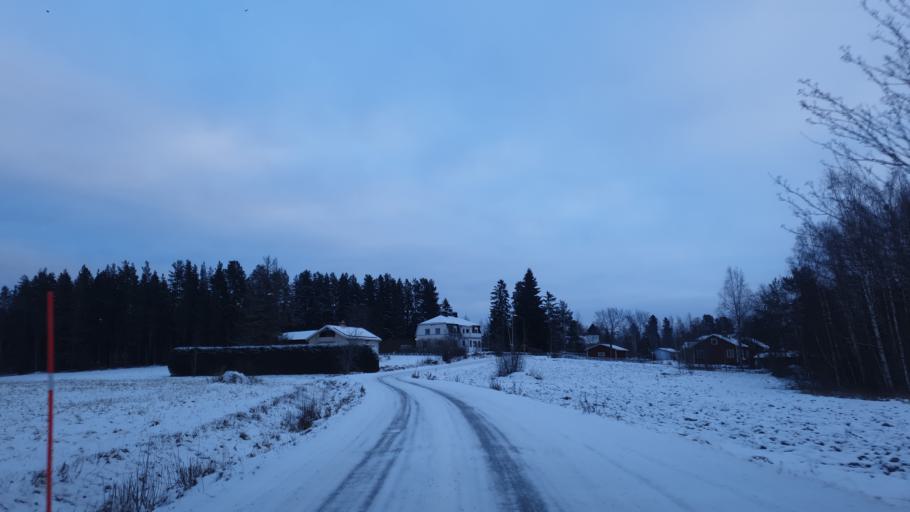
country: SE
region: Gaevleborg
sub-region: Bollnas Kommun
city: Kilafors
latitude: 61.2531
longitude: 16.5462
